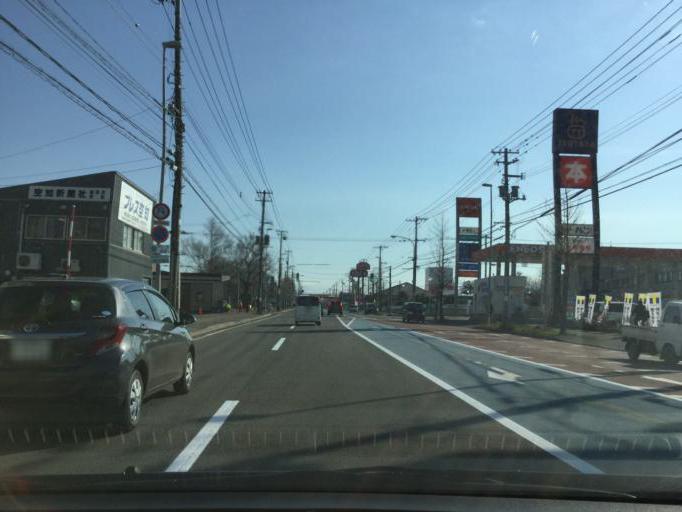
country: JP
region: Hokkaido
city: Iwamizawa
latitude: 43.1978
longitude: 141.7722
